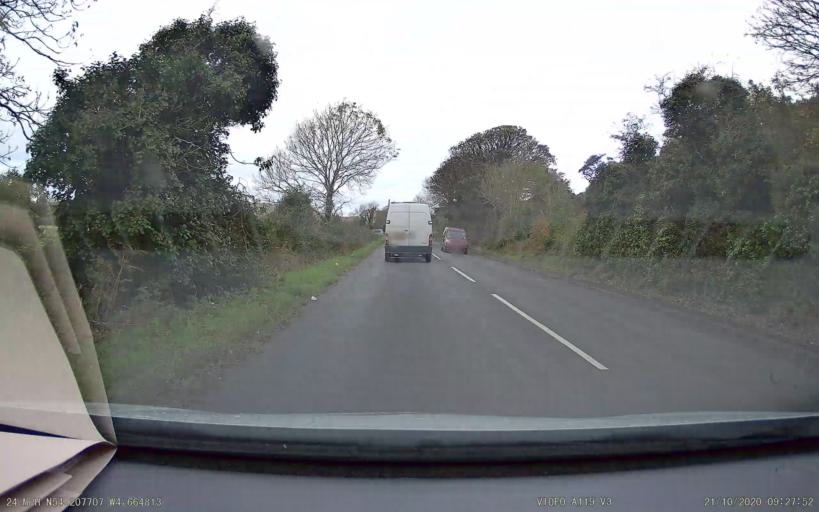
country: IM
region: Castletown
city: Castletown
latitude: 54.2077
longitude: -4.6648
